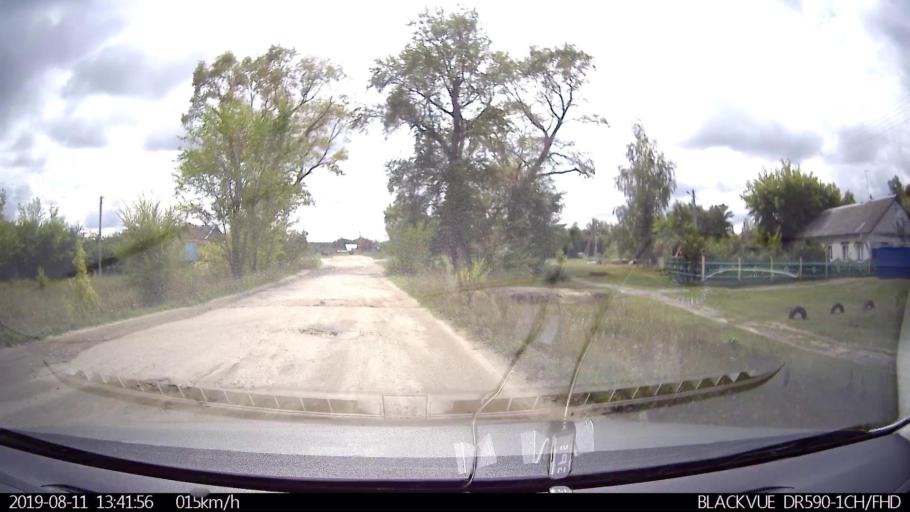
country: RU
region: Ulyanovsk
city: Ignatovka
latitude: 53.8568
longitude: 47.5755
